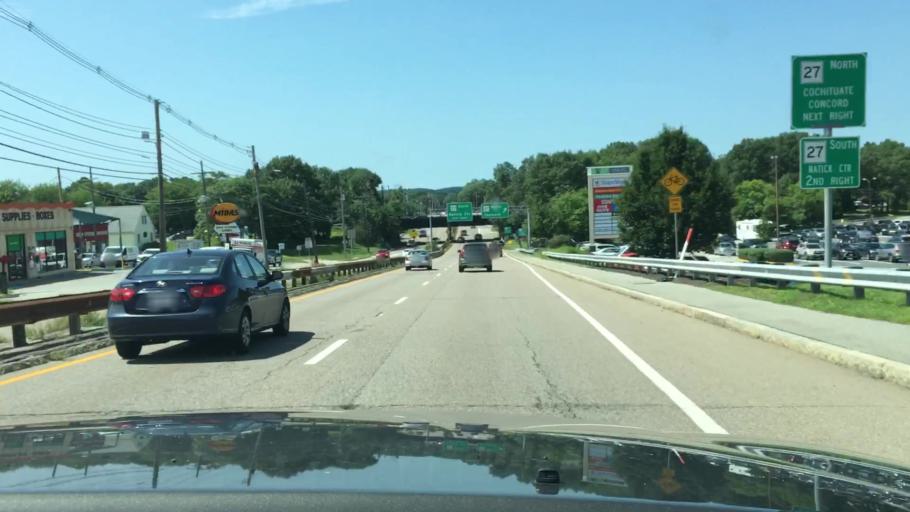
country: US
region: Massachusetts
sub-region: Middlesex County
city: Natick
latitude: 42.3004
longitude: -71.3571
